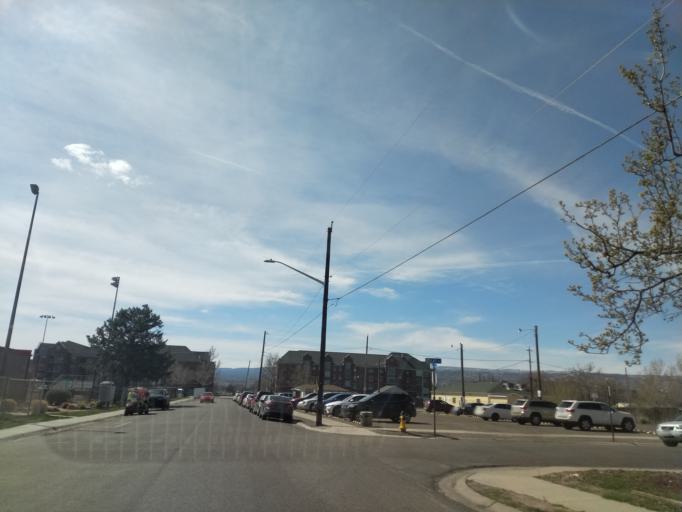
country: US
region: Colorado
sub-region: Mesa County
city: Grand Junction
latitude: 39.0838
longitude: -108.5570
